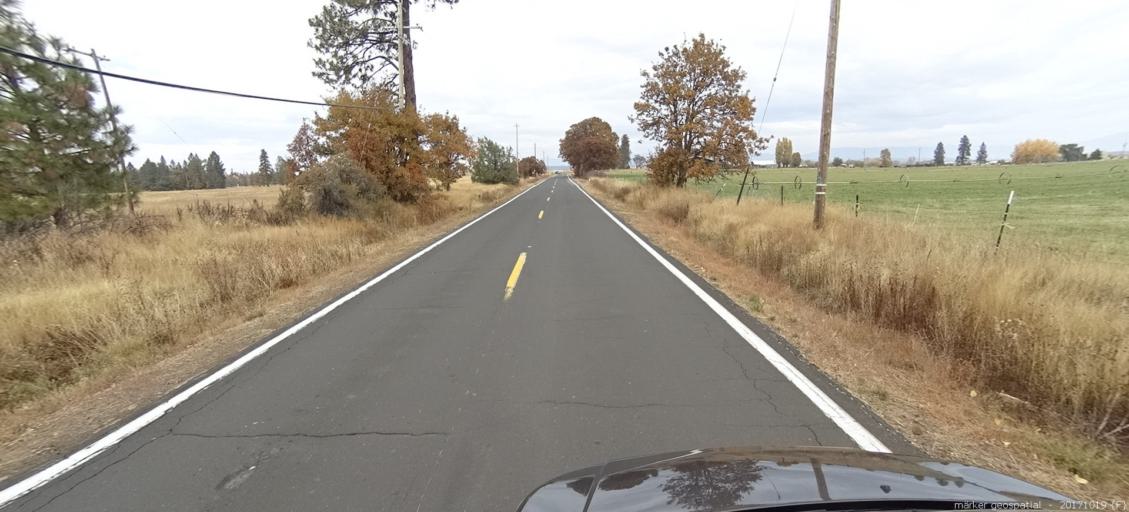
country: US
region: California
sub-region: Shasta County
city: Burney
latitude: 41.0763
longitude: -121.5093
